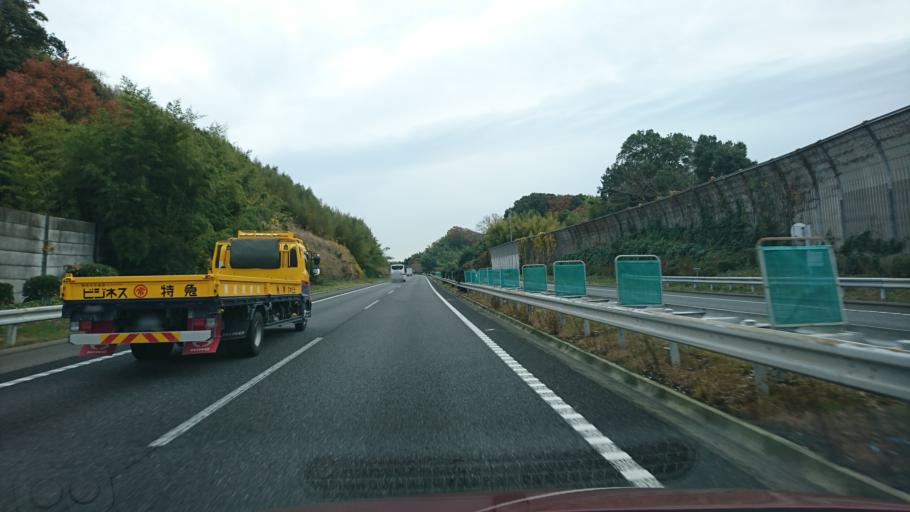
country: JP
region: Hyogo
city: Sandacho
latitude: 34.8217
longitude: 135.1311
